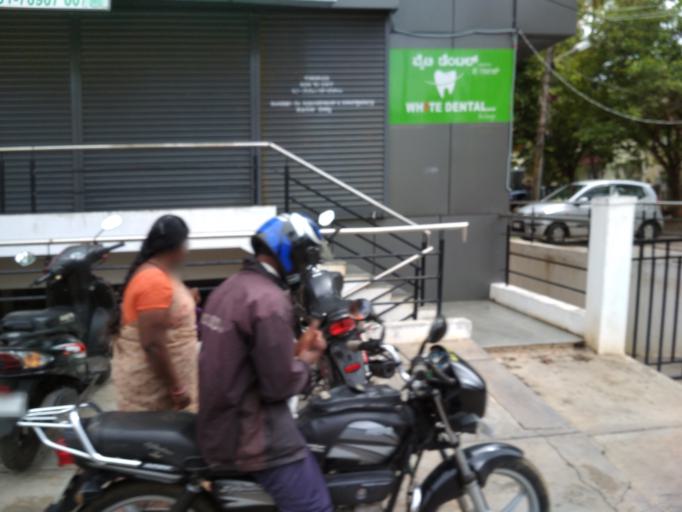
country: IN
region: Karnataka
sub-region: Mysore
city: Mysore
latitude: 12.3249
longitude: 76.6270
